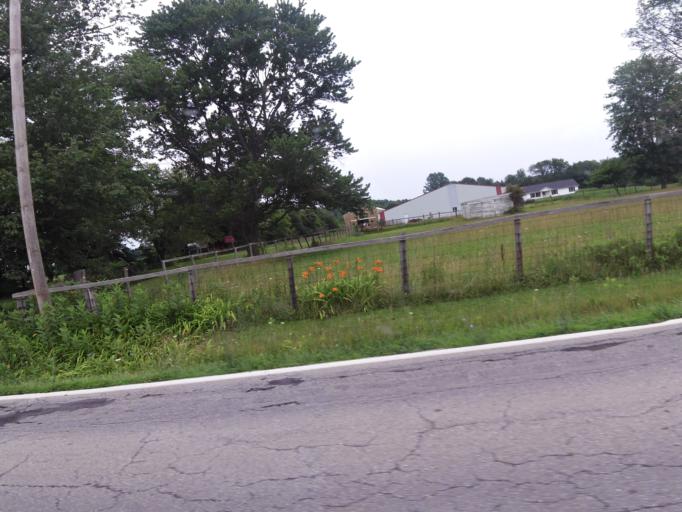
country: US
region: Ohio
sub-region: Clinton County
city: Blanchester
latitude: 39.2713
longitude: -83.9021
